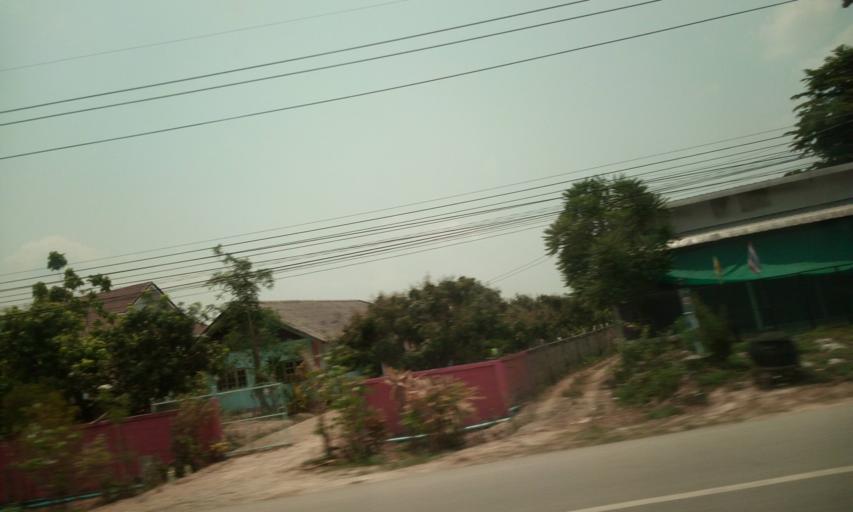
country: TH
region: Chiang Rai
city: Thoeng
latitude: 19.6818
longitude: 100.1278
